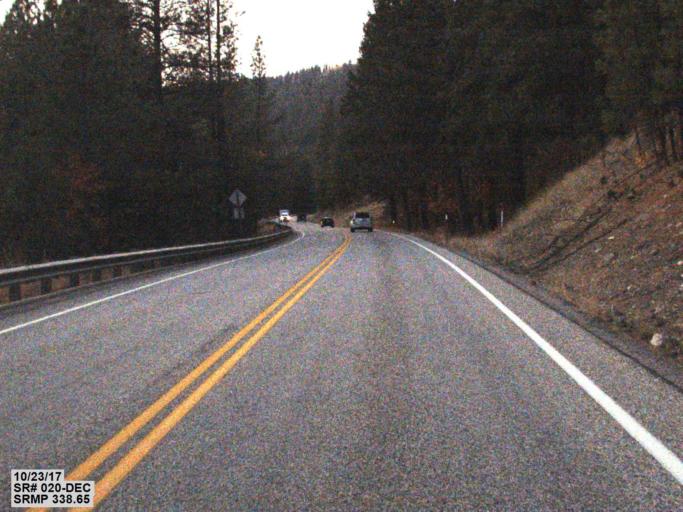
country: US
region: Washington
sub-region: Stevens County
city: Kettle Falls
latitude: 48.5886
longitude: -118.1545
